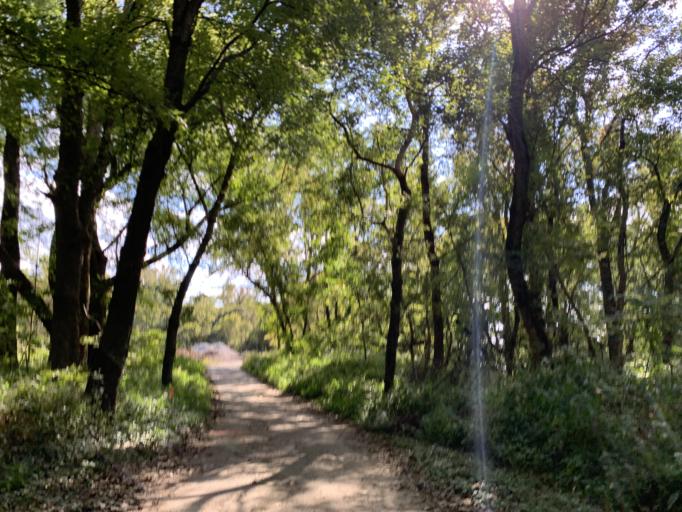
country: US
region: Indiana
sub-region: Floyd County
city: New Albany
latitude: 38.2642
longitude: -85.8304
